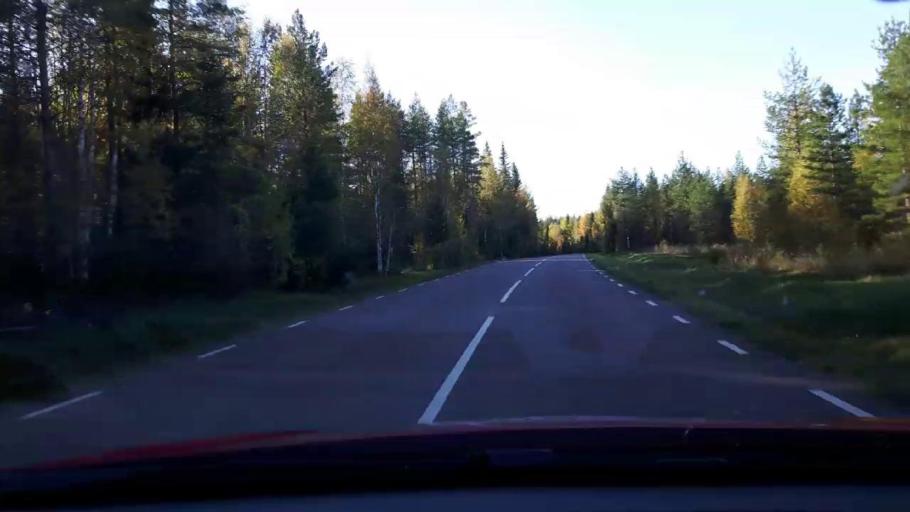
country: SE
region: Jaemtland
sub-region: Stroemsunds Kommun
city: Stroemsund
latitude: 63.8429
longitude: 15.4266
